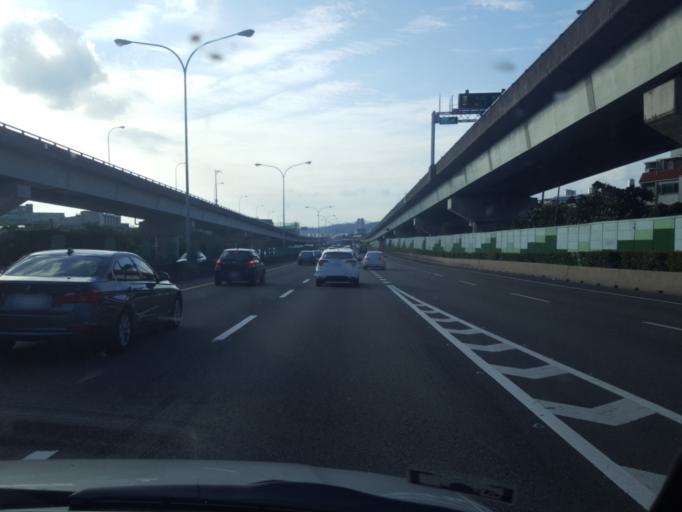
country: TW
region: Taipei
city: Taipei
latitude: 25.0660
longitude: 121.5877
